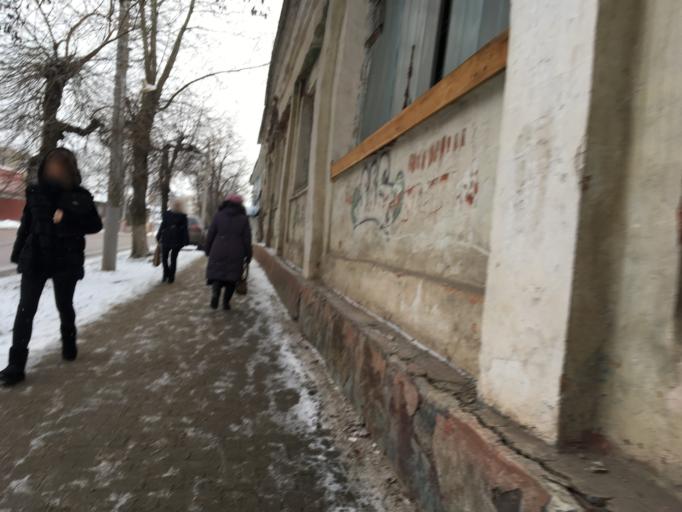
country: RU
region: Tula
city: Tula
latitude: 54.2070
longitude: 37.6129
